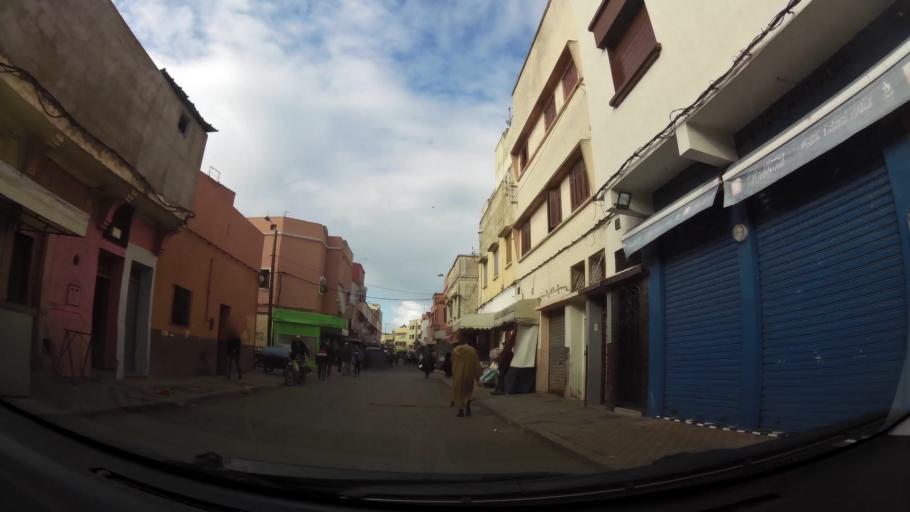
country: MA
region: Doukkala-Abda
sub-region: El-Jadida
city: El Jadida
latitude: 33.2525
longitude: -8.5155
